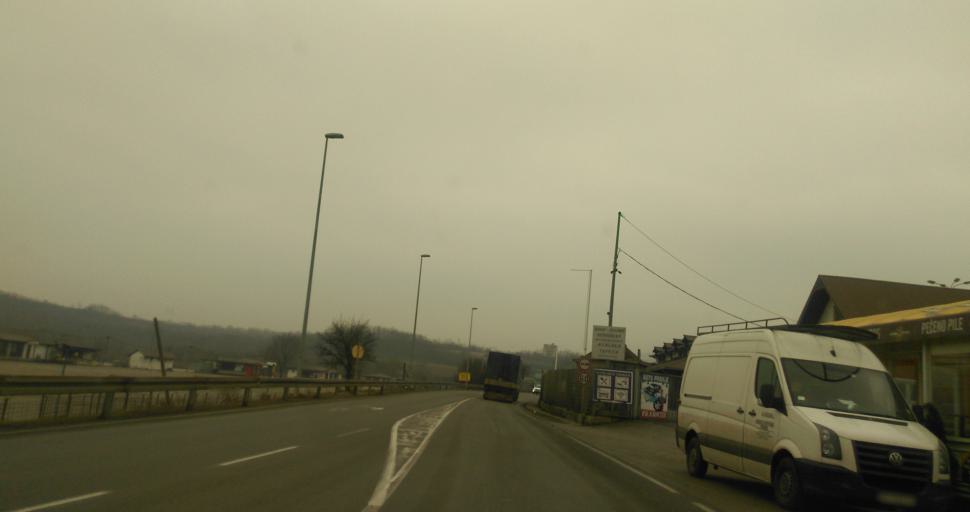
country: RS
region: Central Serbia
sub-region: Belgrade
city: Zvezdara
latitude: 44.7223
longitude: 20.5412
